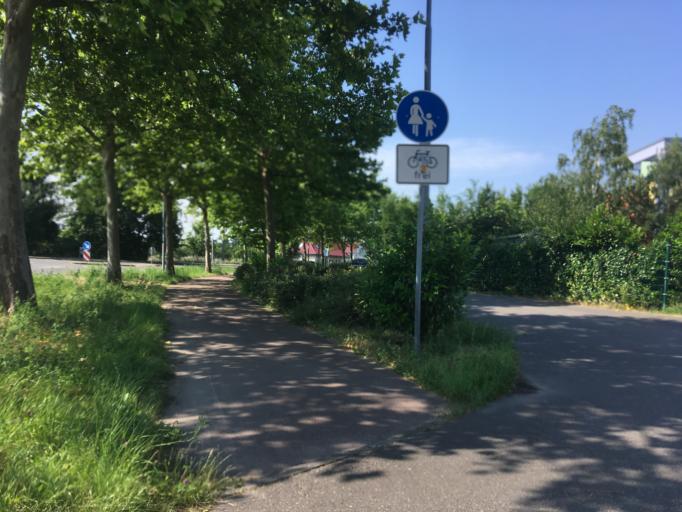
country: DE
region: Saxony-Anhalt
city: Dessau
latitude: 51.8145
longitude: 12.2240
